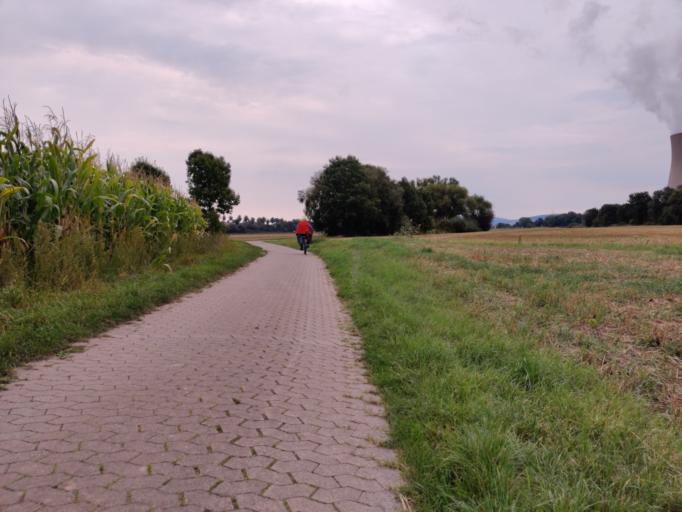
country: DE
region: Lower Saxony
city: Hameln
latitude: 52.0442
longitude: 9.4104
